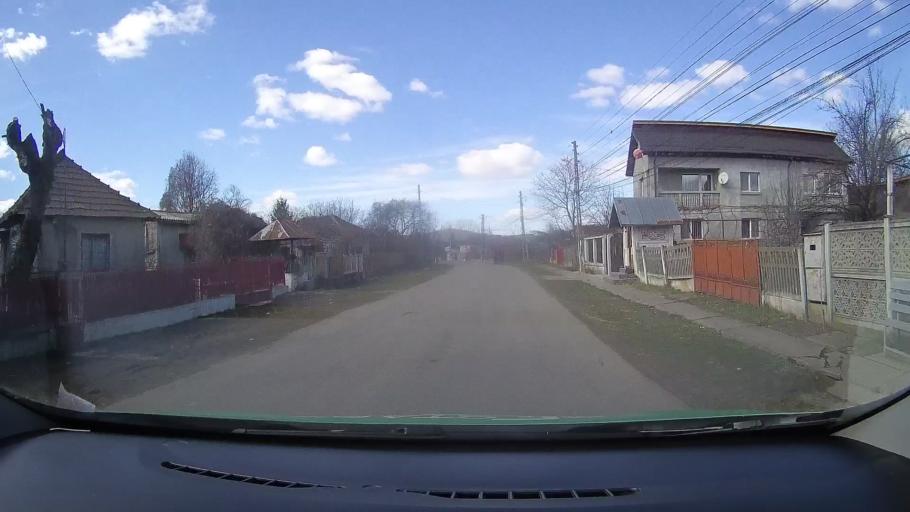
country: RO
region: Dambovita
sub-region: Comuna Doicesti
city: Doicesti
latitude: 44.9920
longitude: 25.3979
